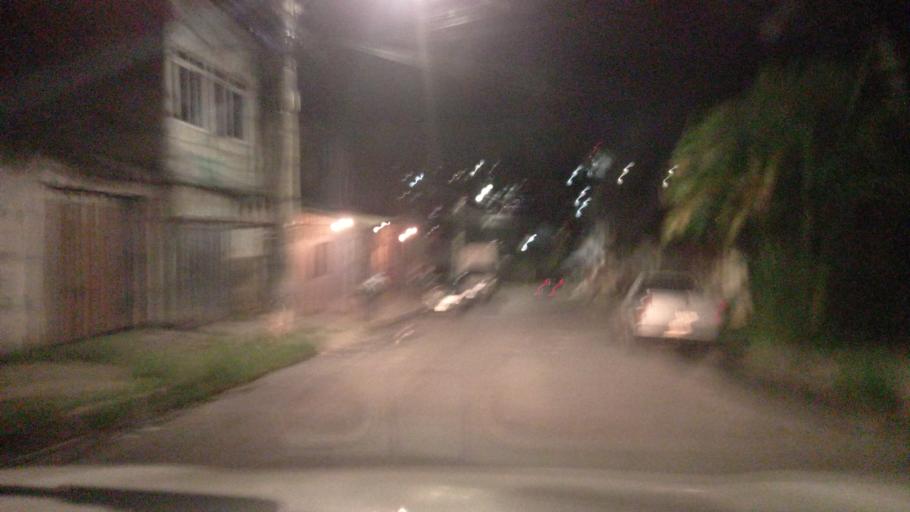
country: BR
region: Minas Gerais
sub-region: Belo Horizonte
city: Belo Horizonte
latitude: -19.8761
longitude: -43.9428
